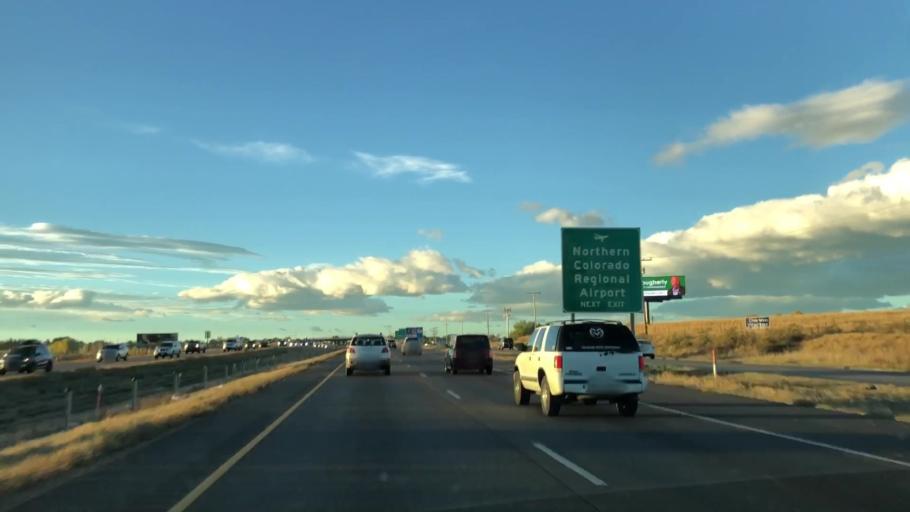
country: US
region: Colorado
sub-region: Weld County
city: Windsor
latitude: 40.4886
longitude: -104.9929
